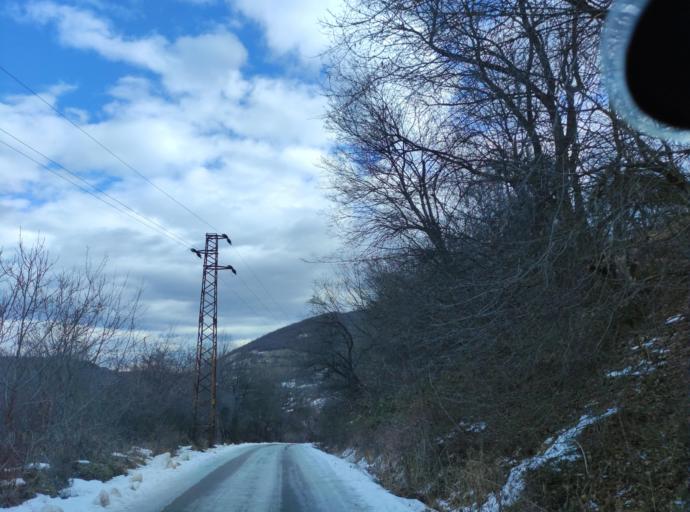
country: BG
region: Montana
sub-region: Obshtina Chiprovtsi
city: Chiprovtsi
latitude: 43.3774
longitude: 22.8708
